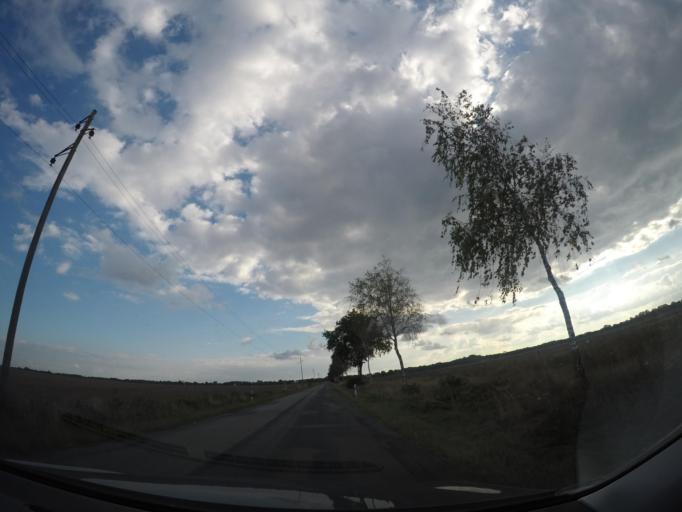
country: DE
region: Saxony-Anhalt
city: Mieste
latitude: 52.5178
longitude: 11.1469
